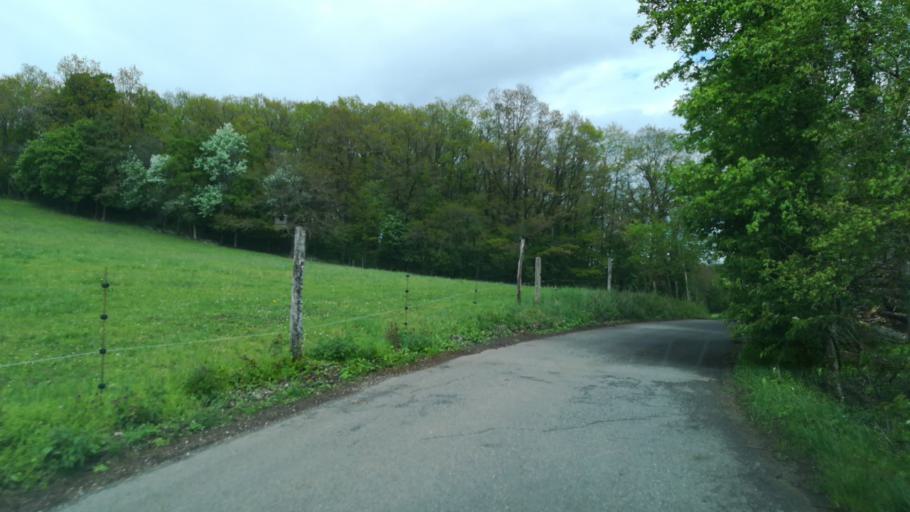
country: CH
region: Schaffhausen
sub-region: Bezirk Reiat
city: Stetten
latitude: 47.7433
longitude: 8.6686
